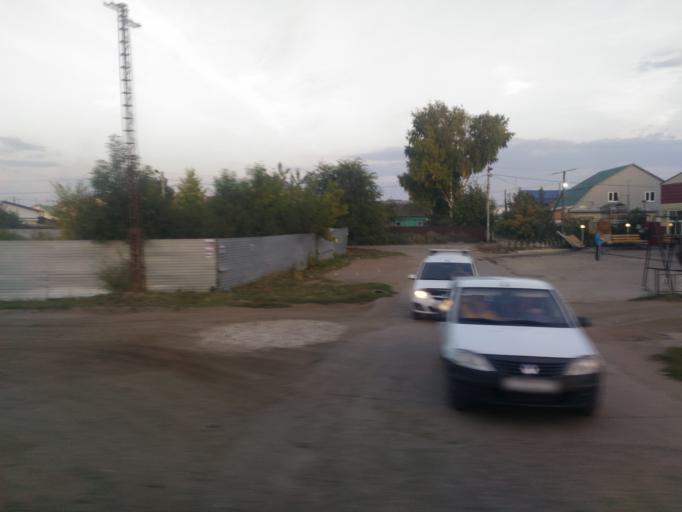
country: RU
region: Ulyanovsk
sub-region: Ulyanovskiy Rayon
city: Ulyanovsk
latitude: 54.2639
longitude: 48.2809
